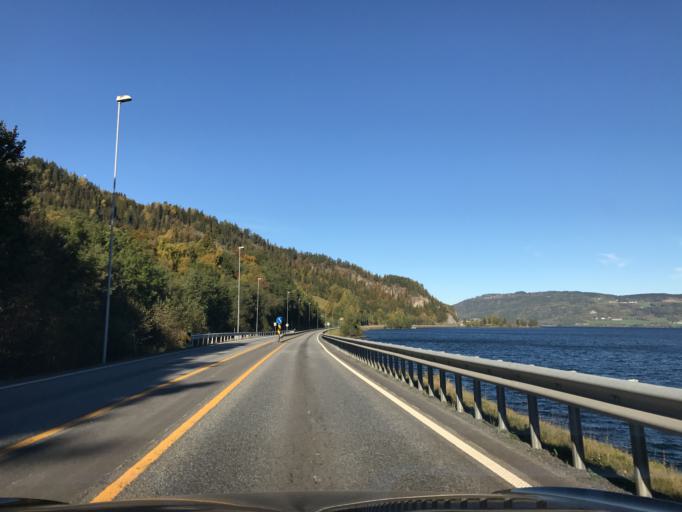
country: NO
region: Hedmark
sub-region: Ringsaker
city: Moelv
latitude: 60.9354
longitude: 10.6501
